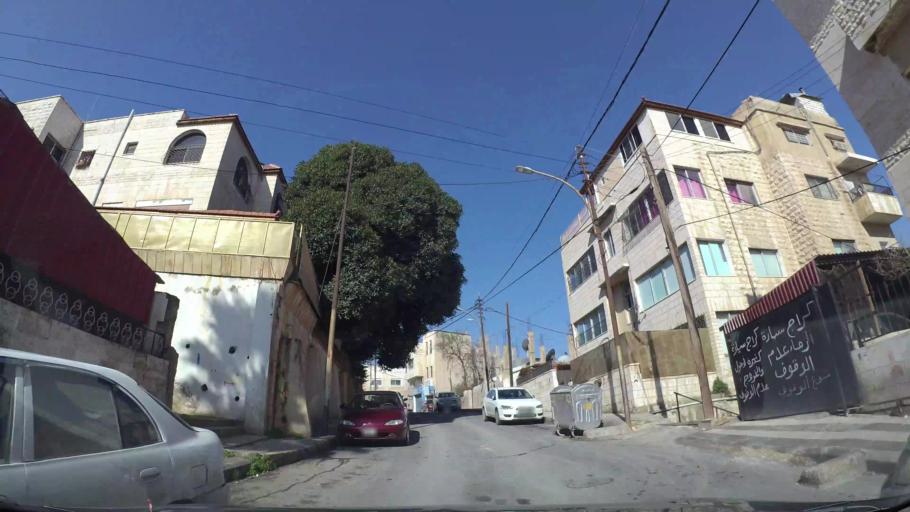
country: JO
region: Amman
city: Amman
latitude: 31.9867
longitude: 35.9908
